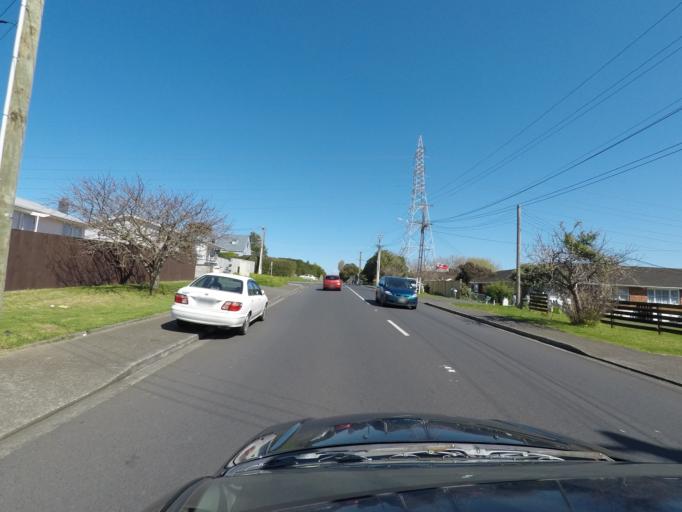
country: NZ
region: Auckland
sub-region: Auckland
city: Tamaki
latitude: -36.9264
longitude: 174.8502
